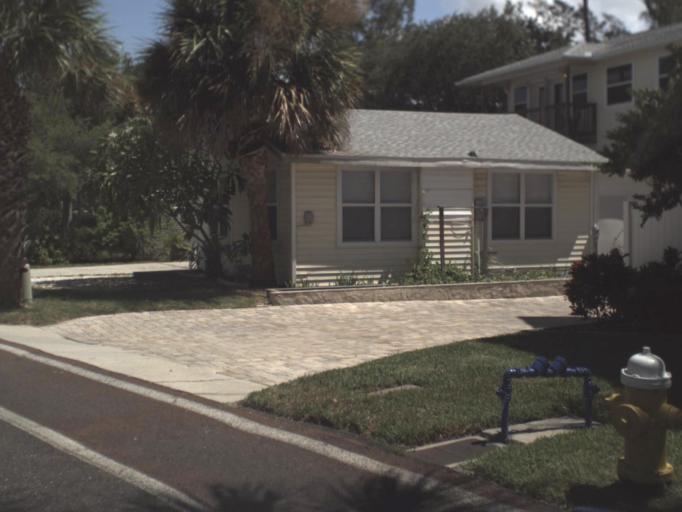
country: US
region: Florida
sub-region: Pinellas County
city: Indian Shores
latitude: 27.8594
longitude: -82.8472
